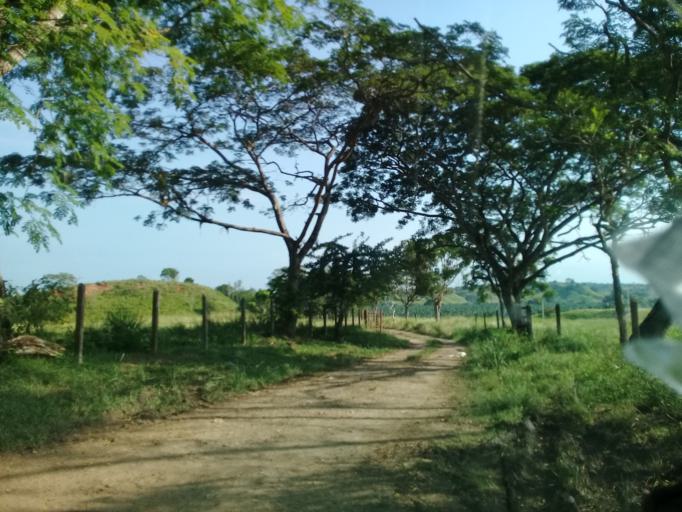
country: CO
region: Antioquia
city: Puerto Triunfo
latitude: 5.7065
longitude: -74.5623
